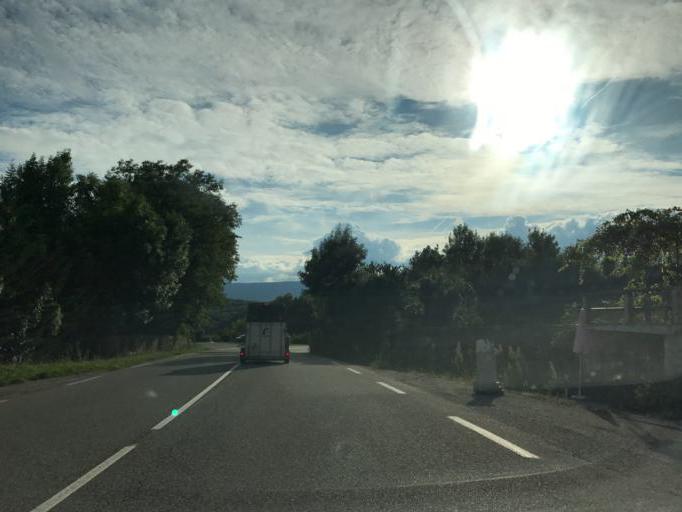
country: FR
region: Rhone-Alpes
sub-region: Departement de l'Ain
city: Bellegarde-sur-Valserine
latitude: 46.0917
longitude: 5.8616
